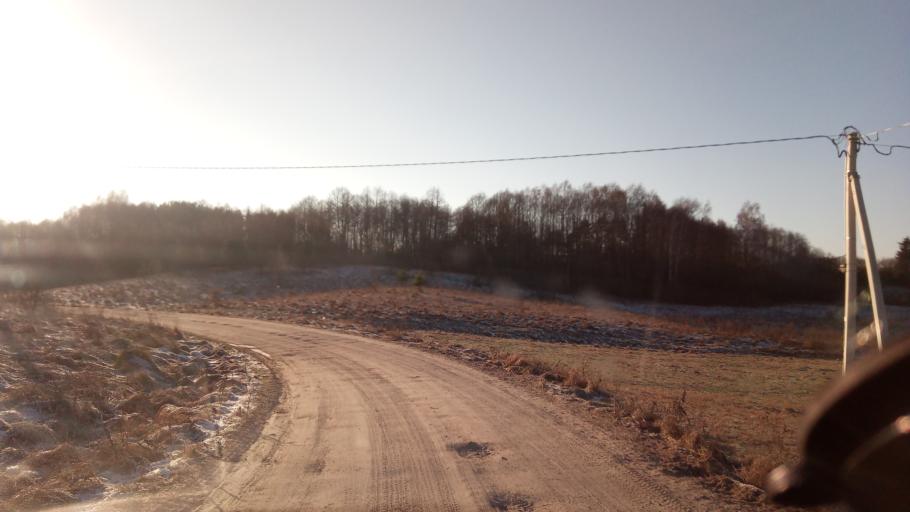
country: LT
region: Alytaus apskritis
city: Druskininkai
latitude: 54.1056
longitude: 24.0117
